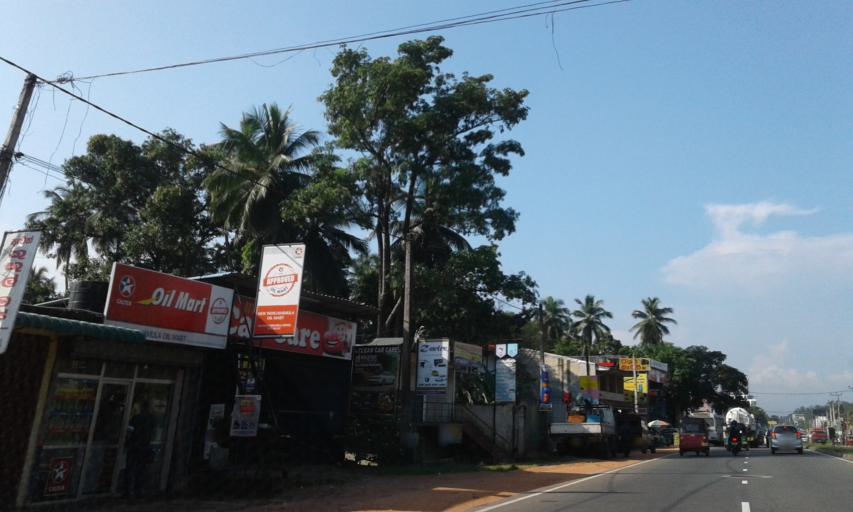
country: LK
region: Western
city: Gampaha
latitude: 7.0284
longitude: 79.9821
